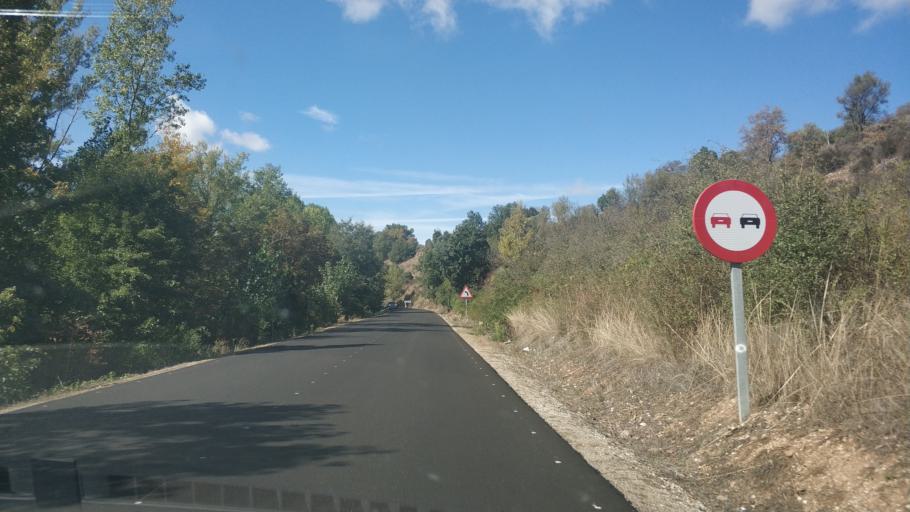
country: ES
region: Castille and Leon
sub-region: Provincia de Burgos
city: Covarrubias
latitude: 42.0482
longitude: -3.5395
